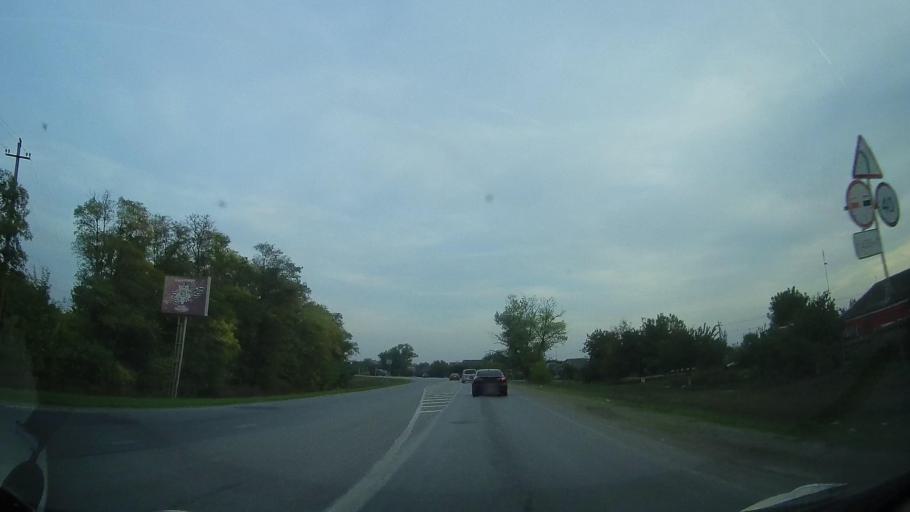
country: RU
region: Rostov
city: Kirovskaya
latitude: 46.9713
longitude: 40.0532
